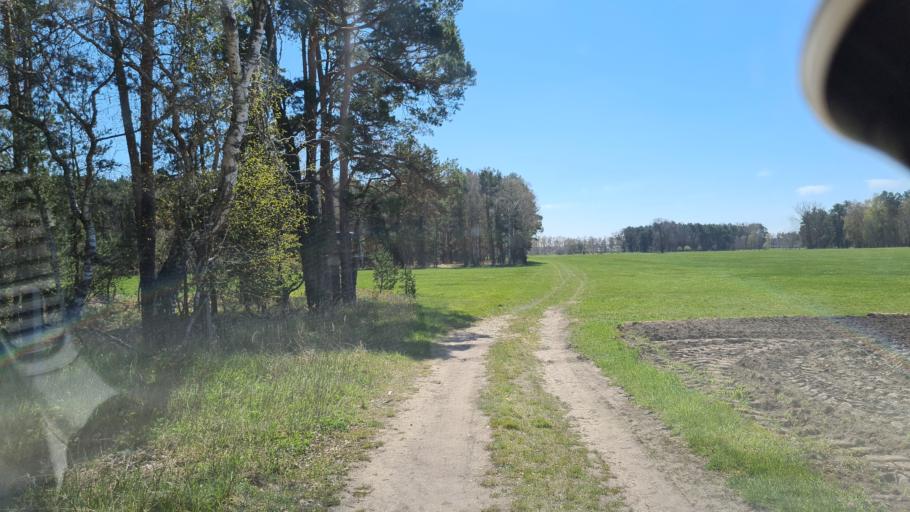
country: DE
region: Brandenburg
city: Ruckersdorf
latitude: 51.5534
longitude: 13.6187
